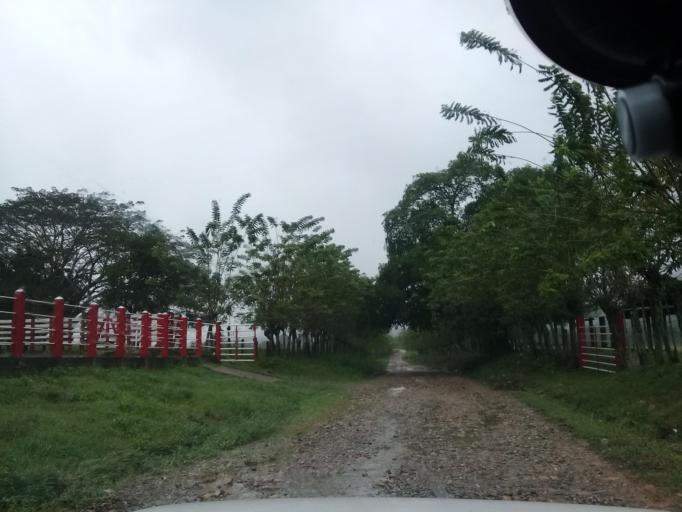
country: MX
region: Veracruz
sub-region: Chalma
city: San Pedro Coyutla
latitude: 21.2401
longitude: -98.4610
